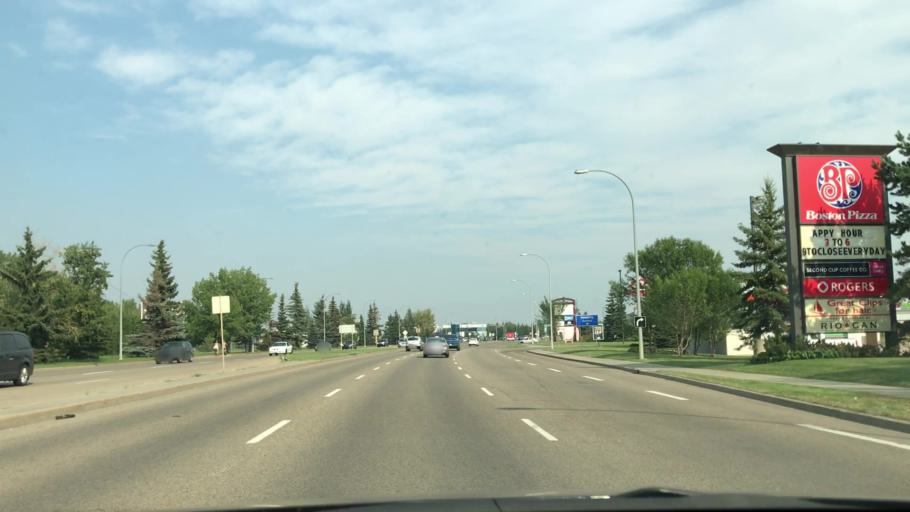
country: CA
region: Alberta
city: Edmonton
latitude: 53.4539
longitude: -113.4849
